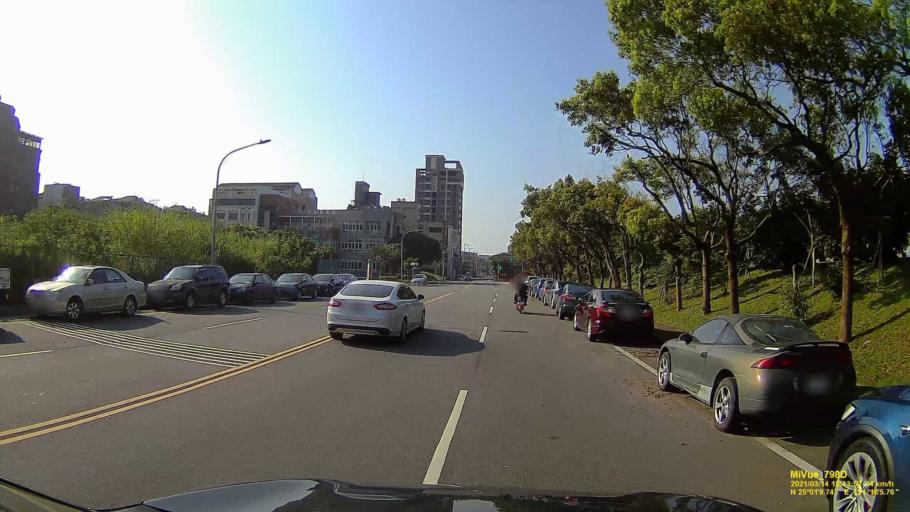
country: TW
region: Taiwan
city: Taoyuan City
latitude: 25.0196
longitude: 121.2681
